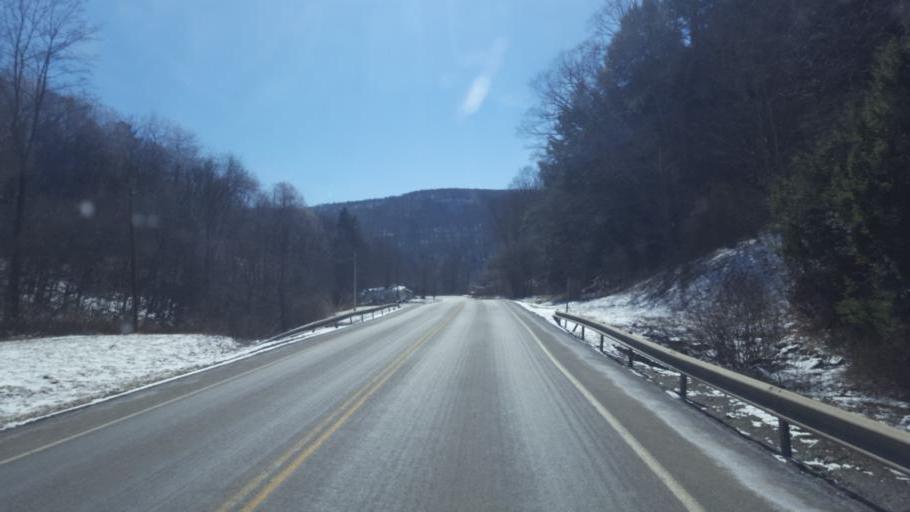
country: US
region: New York
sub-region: Allegany County
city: Andover
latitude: 42.0417
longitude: -77.7862
